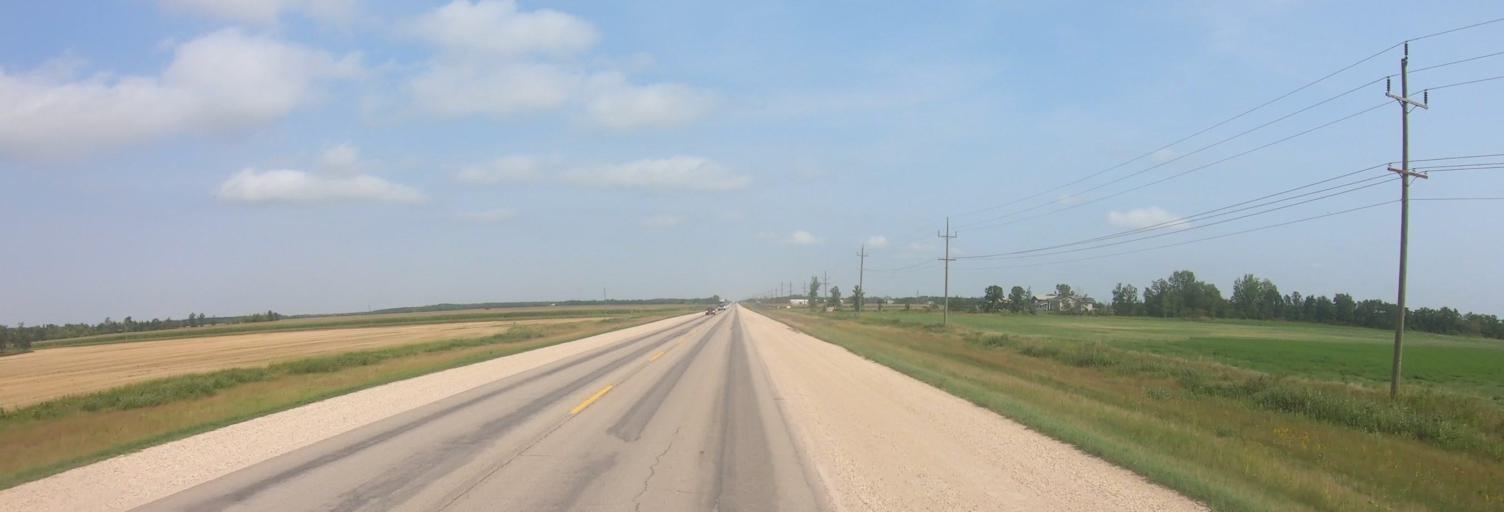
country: CA
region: Manitoba
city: Steinbach
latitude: 49.4637
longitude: -96.6911
